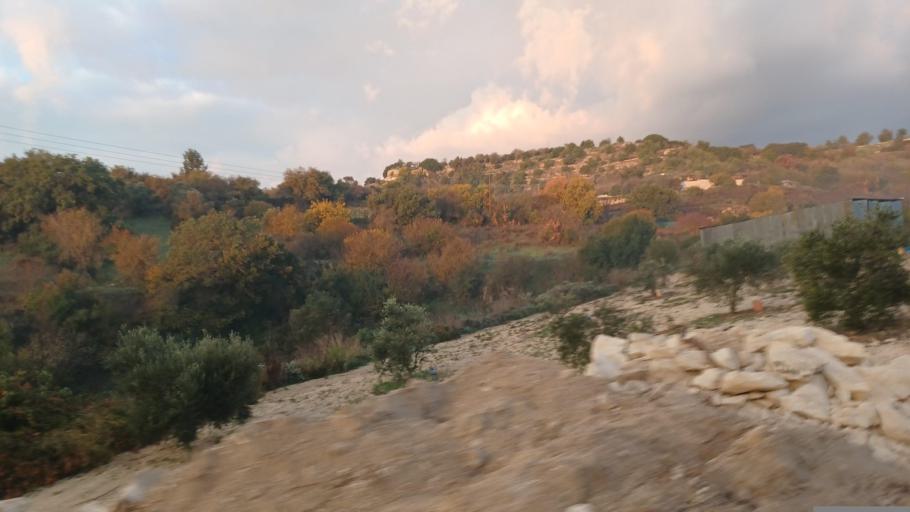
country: CY
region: Pafos
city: Mesogi
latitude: 34.8511
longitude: 32.5180
